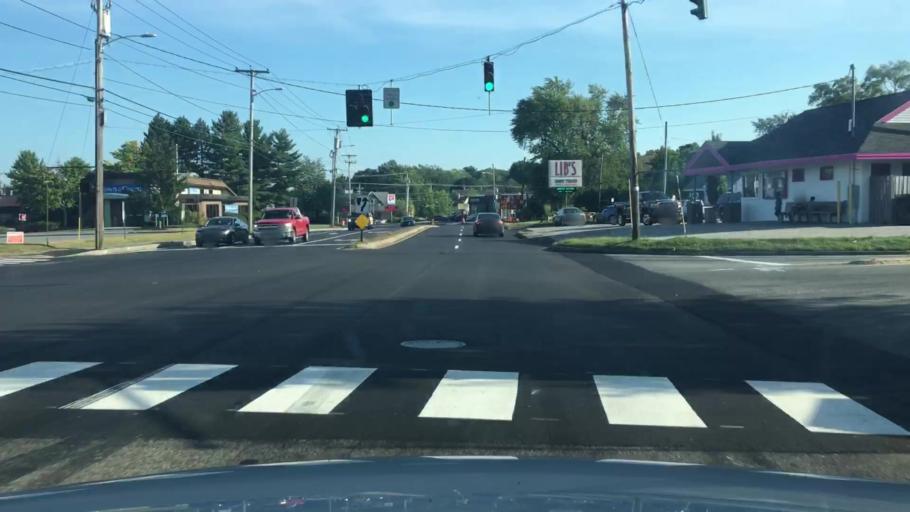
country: US
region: Maine
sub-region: Cumberland County
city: Portland
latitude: 43.7017
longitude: -70.2891
